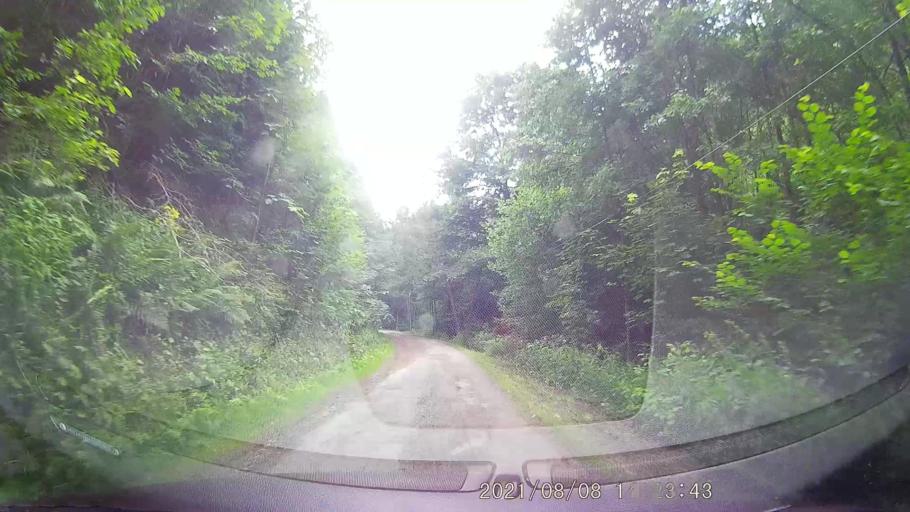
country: PL
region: Lower Silesian Voivodeship
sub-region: Powiat klodzki
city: Lewin Klodzki
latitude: 50.4430
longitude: 16.3013
